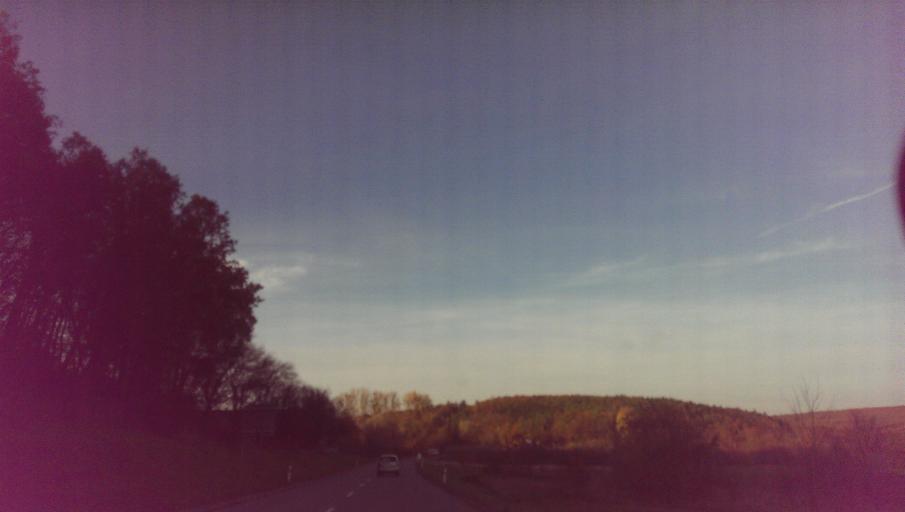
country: CZ
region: Zlin
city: Brezolupy
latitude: 49.1274
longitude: 17.5890
